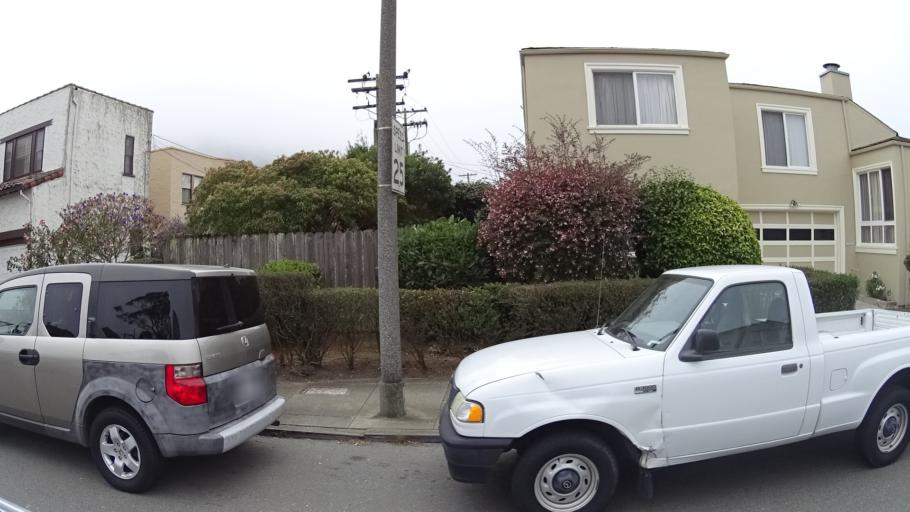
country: US
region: California
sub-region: San Mateo County
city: Daly City
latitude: 37.7432
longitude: -122.4532
